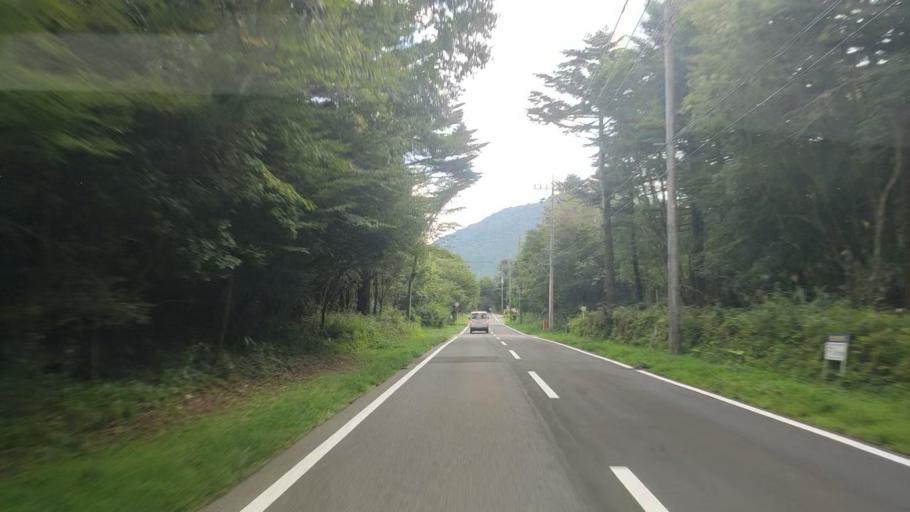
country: JP
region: Shizuoka
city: Gotemba
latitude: 35.2661
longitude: 138.8053
